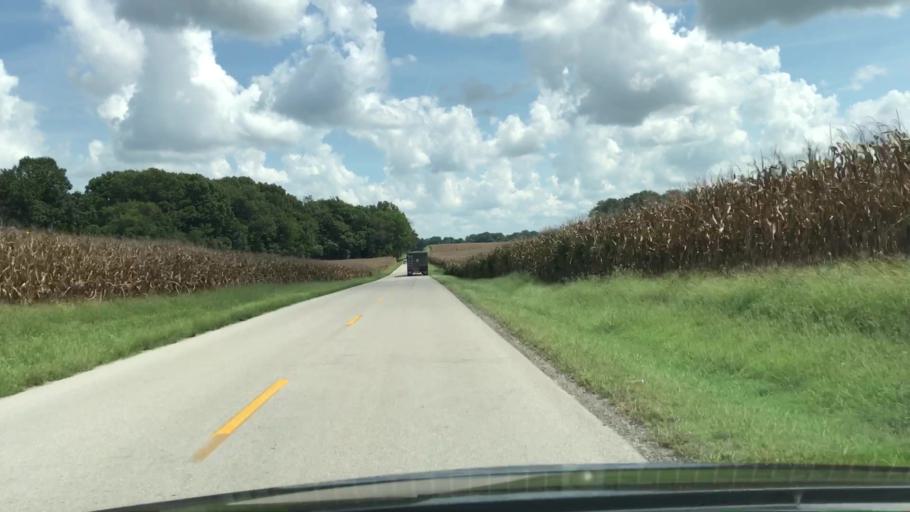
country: US
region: Kentucky
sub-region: Todd County
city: Guthrie
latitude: 36.6492
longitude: -86.9914
